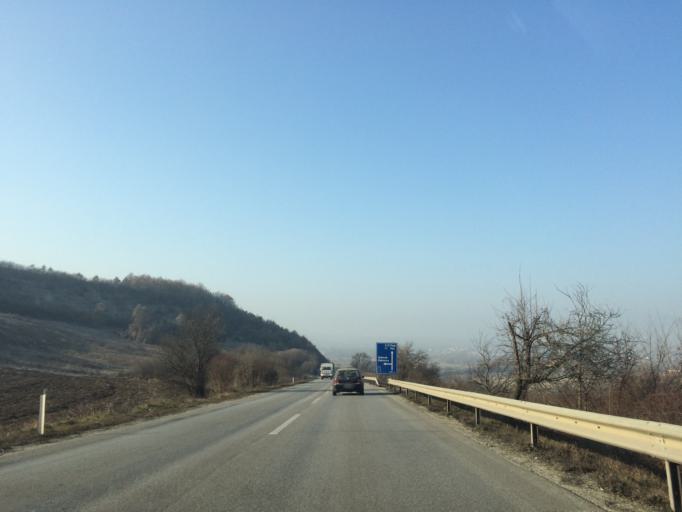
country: XK
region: Pec
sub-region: Komuna e Klines
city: Klina
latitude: 42.5924
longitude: 20.5903
